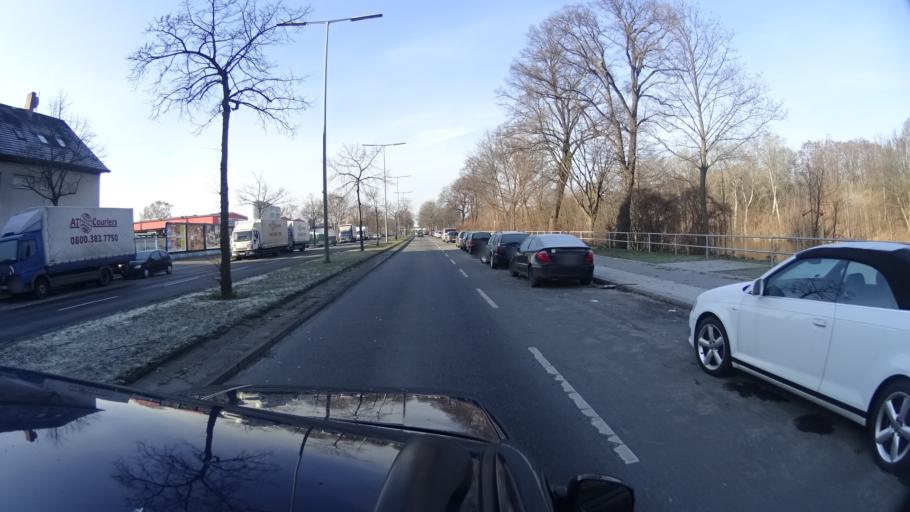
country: DE
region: Berlin
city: Charlottenburg-Nord
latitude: 52.5479
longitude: 13.3075
